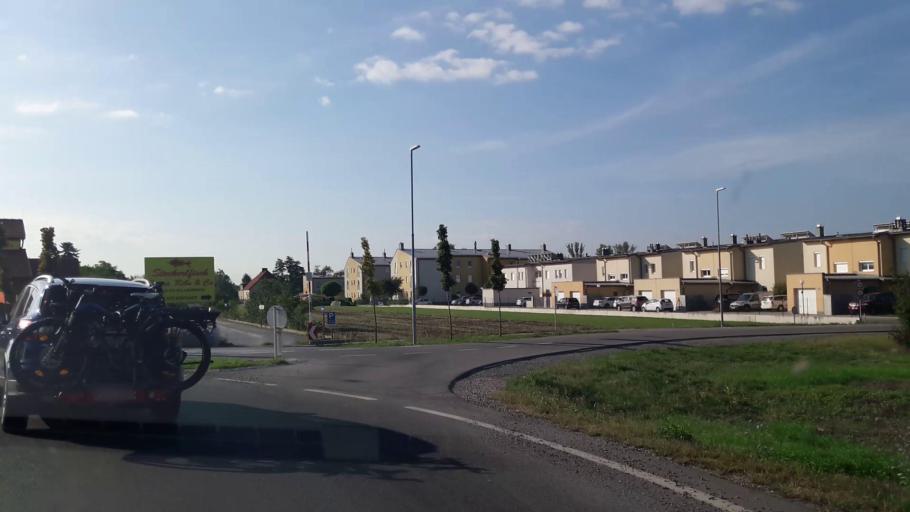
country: AT
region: Burgenland
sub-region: Eisenstadt-Umgebung
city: Trausdorf an der Wulka
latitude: 47.8160
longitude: 16.5469
